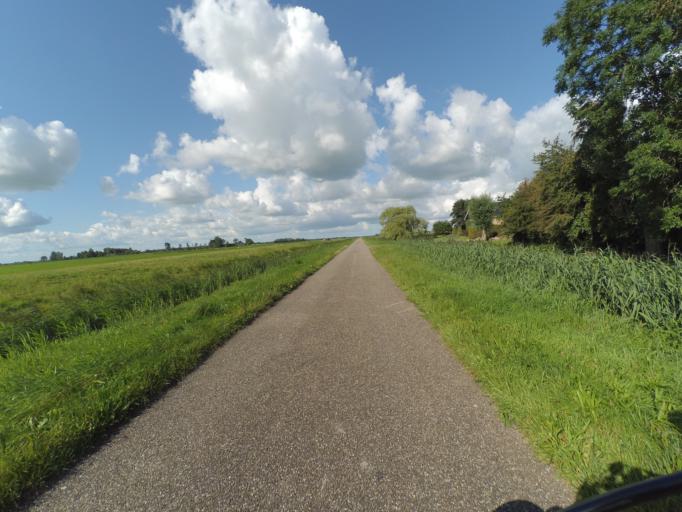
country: NL
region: Friesland
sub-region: Gemeente Dantumadiel
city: Feanwalden
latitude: 53.2509
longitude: 5.9748
